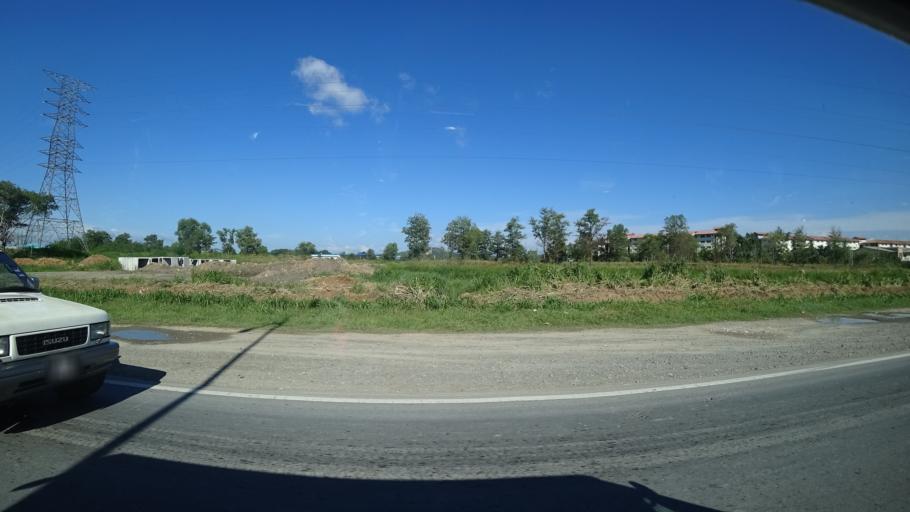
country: MY
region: Sabah
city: Kota Kinabalu
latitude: 6.1126
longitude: 116.2048
